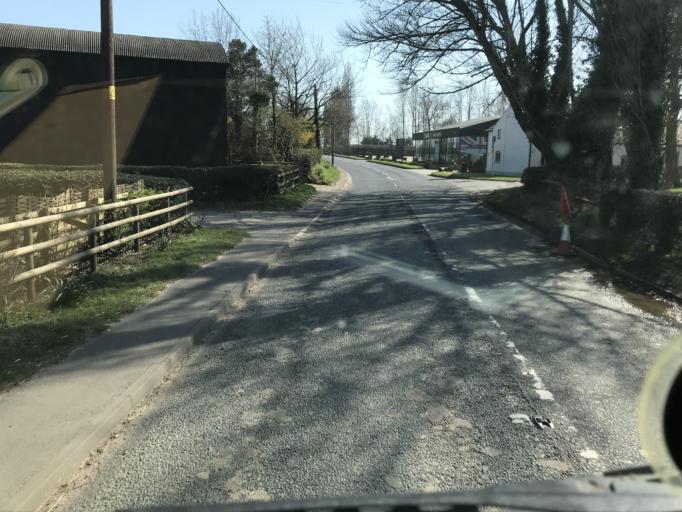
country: GB
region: England
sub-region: Cheshire East
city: Mobberley
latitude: 53.2848
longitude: -2.3298
